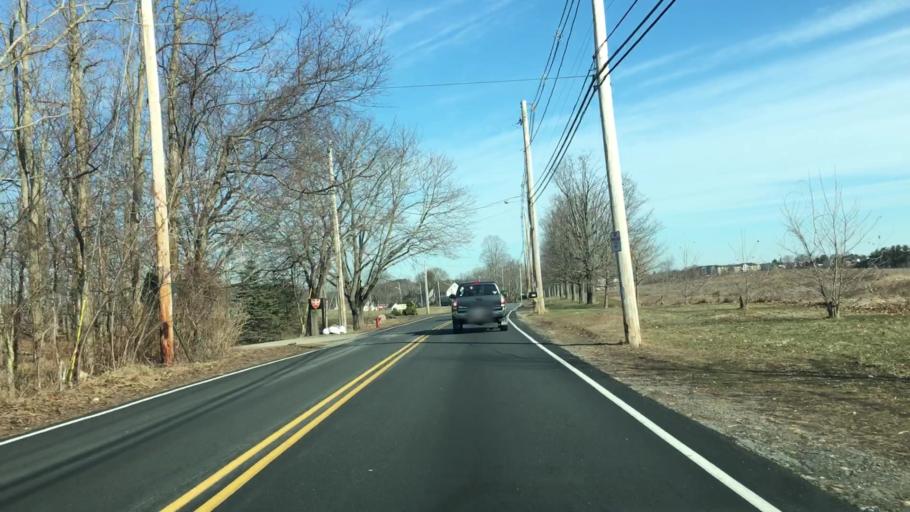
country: US
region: Massachusetts
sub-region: Essex County
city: Amesbury
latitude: 42.8562
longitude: -70.9527
